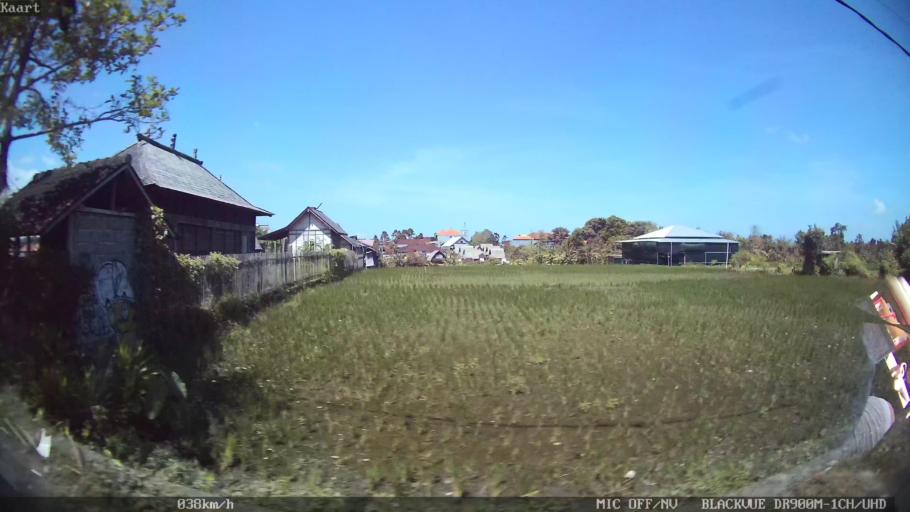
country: ID
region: Bali
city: Denpasar
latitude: -8.6666
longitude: 115.1675
